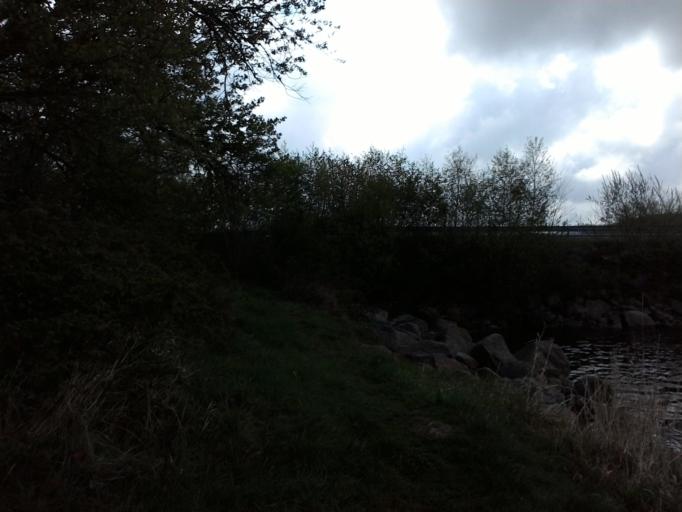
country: FR
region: Bourgogne
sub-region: Departement de la Cote-d'Or
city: Saulieu
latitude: 47.2515
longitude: 4.1893
